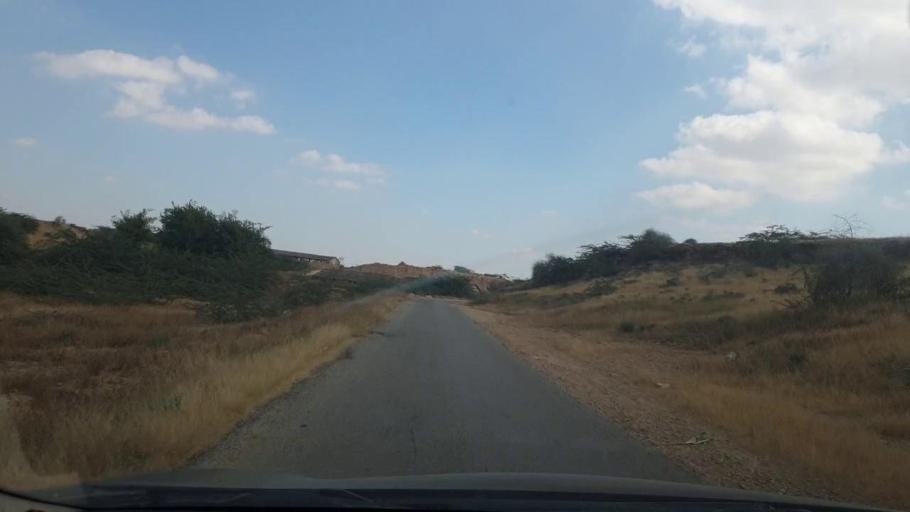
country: PK
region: Sindh
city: Malir Cantonment
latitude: 25.0247
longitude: 67.3513
